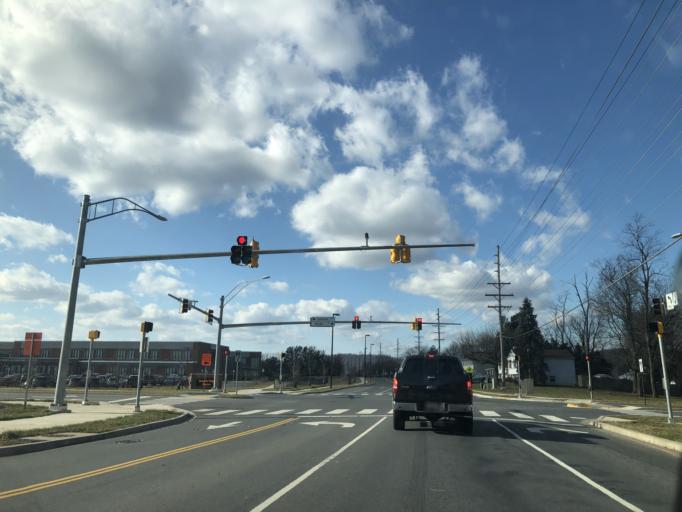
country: US
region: Maryland
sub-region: Frederick County
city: Ballenger Creek
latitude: 39.4092
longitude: -77.4533
